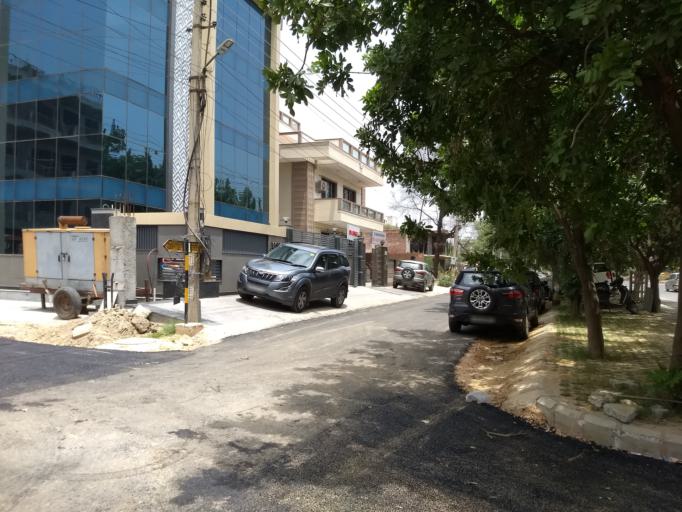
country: IN
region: Haryana
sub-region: Gurgaon
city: Gurgaon
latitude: 28.4486
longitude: 77.0829
